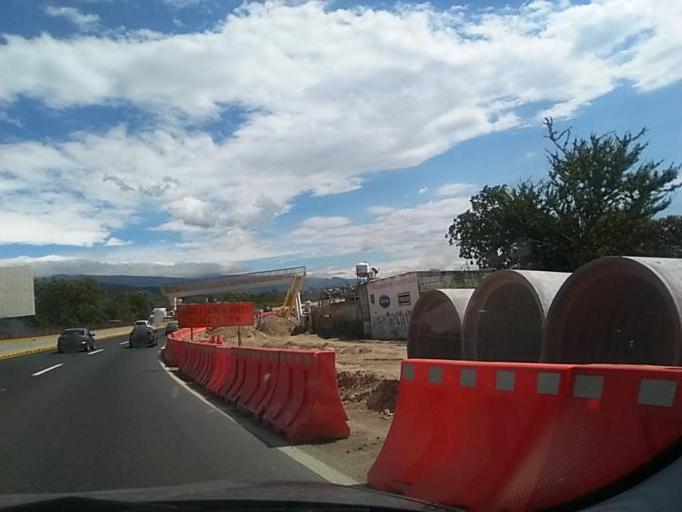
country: MX
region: Morelos
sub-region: Cuernavaca
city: Colonia los Cerritos
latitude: 18.9596
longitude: -99.2192
